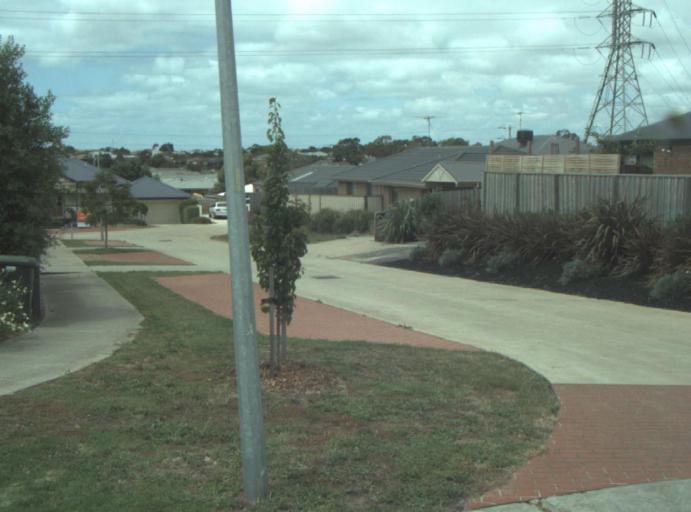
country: AU
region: Victoria
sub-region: Greater Geelong
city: Wandana Heights
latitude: -38.1952
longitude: 144.3145
